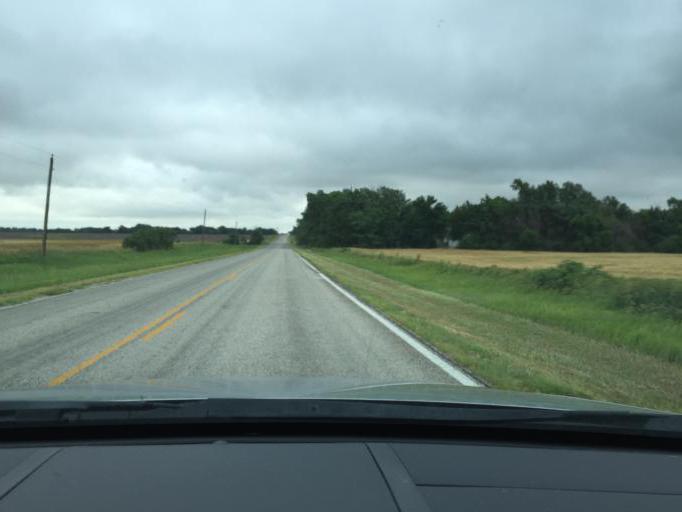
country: US
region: Kansas
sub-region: McPherson County
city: Moundridge
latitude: 38.2031
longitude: -97.6331
